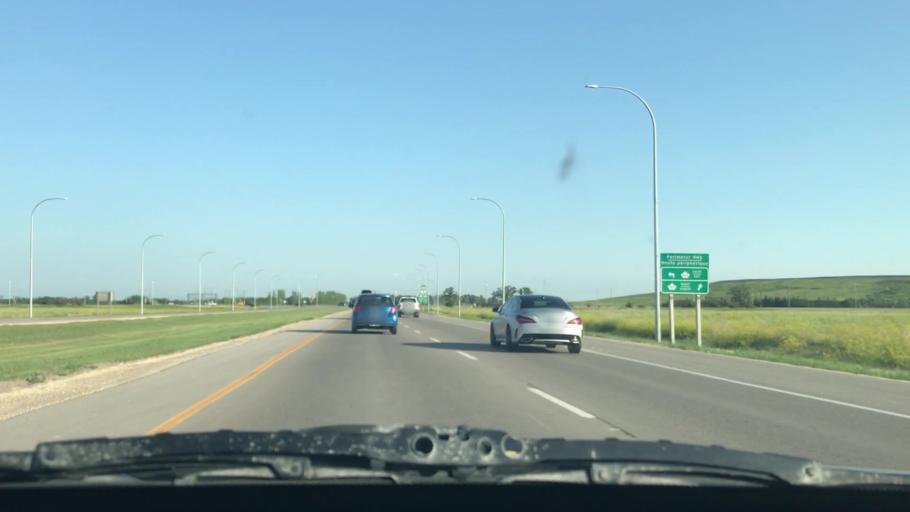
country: CA
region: Manitoba
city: Winnipeg
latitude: 49.7723
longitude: -97.1853
